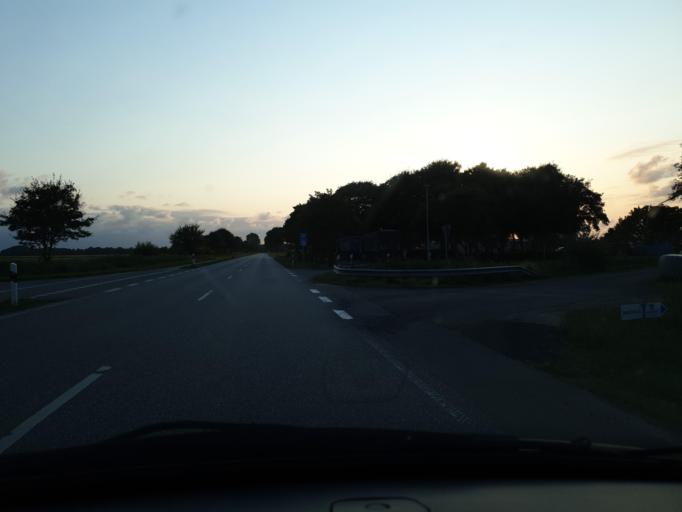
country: DE
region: Schleswig-Holstein
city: Schmedeswurth
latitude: 53.9072
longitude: 9.0761
